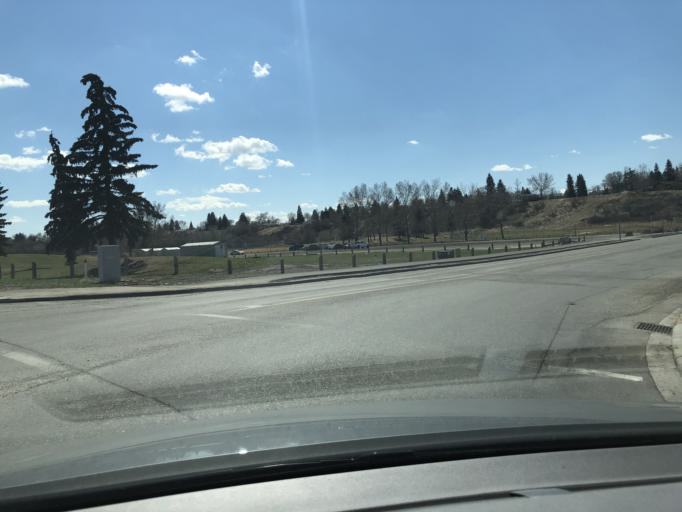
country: CA
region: Alberta
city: Calgary
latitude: 50.9997
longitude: -114.0099
